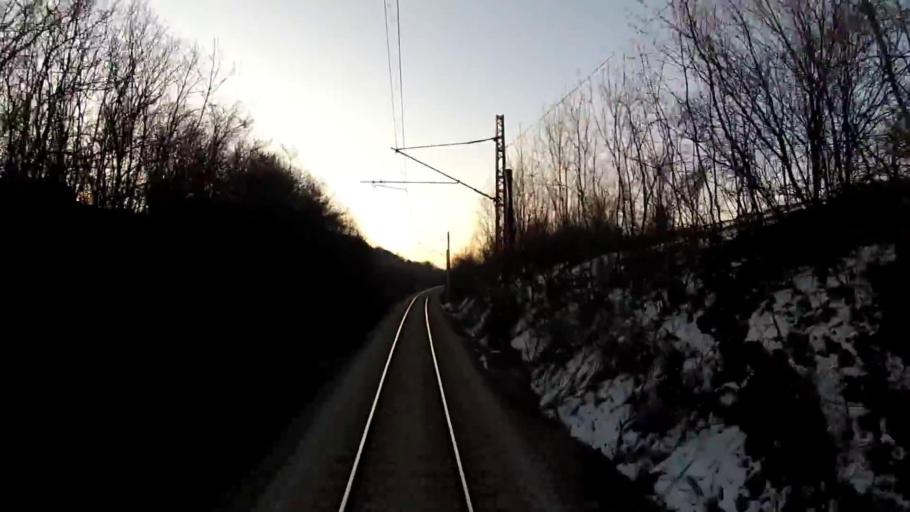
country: BG
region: Sofiya
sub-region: Obshtina Dragoman
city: Dragoman
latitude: 42.9039
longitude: 22.9471
